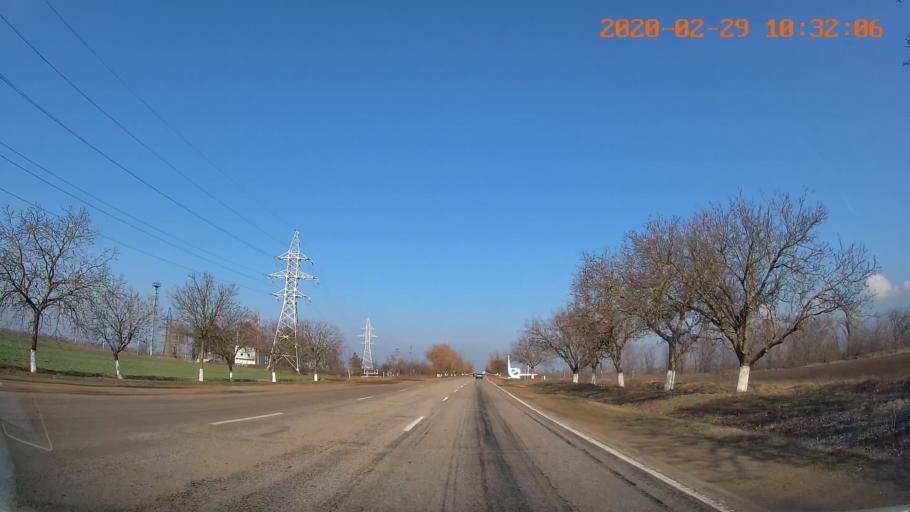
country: UA
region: Odessa
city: Velykoploske
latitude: 46.9571
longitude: 29.5565
